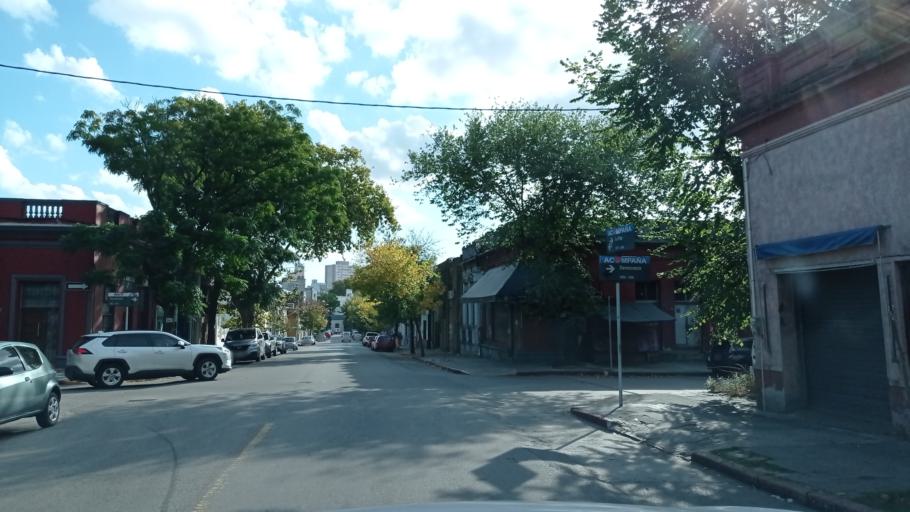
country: UY
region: Montevideo
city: Montevideo
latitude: -34.8945
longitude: -56.1759
